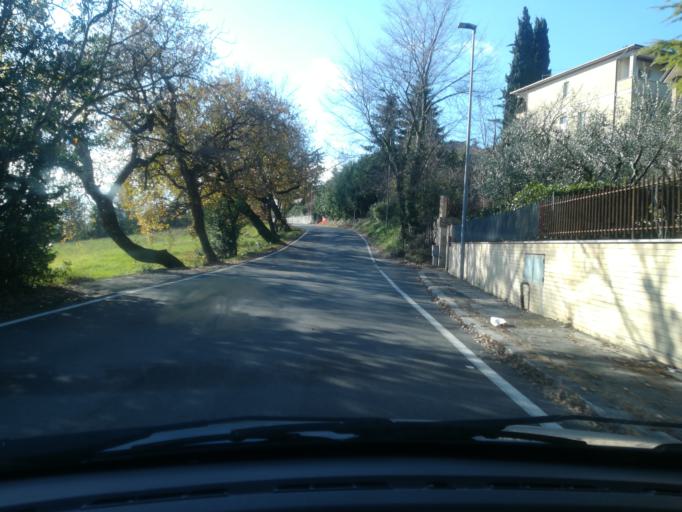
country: IT
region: The Marches
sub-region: Provincia di Macerata
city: Macerata
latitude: 43.2906
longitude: 13.4394
